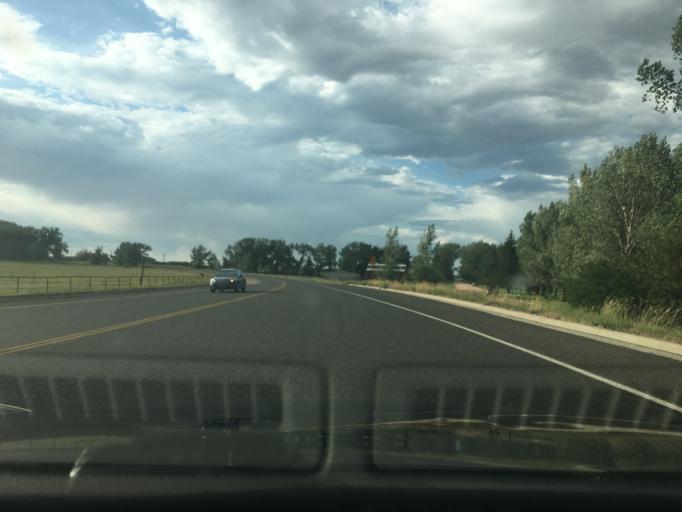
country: US
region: Wyoming
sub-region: Albany County
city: Laramie
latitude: 41.3134
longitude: -105.6293
